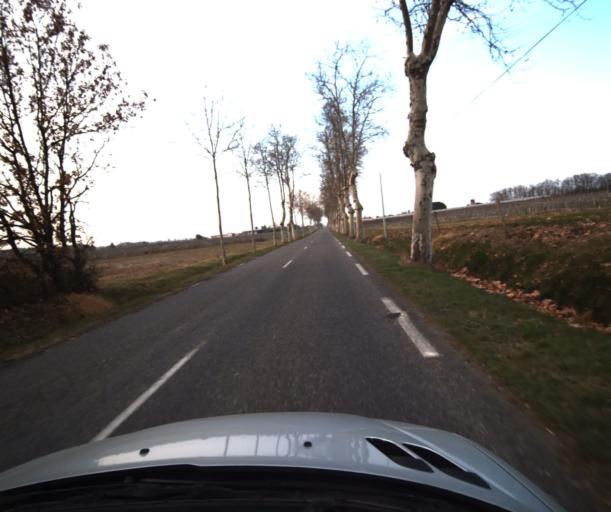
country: FR
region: Midi-Pyrenees
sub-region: Departement du Tarn-et-Garonne
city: Labastide-Saint-Pierre
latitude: 43.8804
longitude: 1.3771
